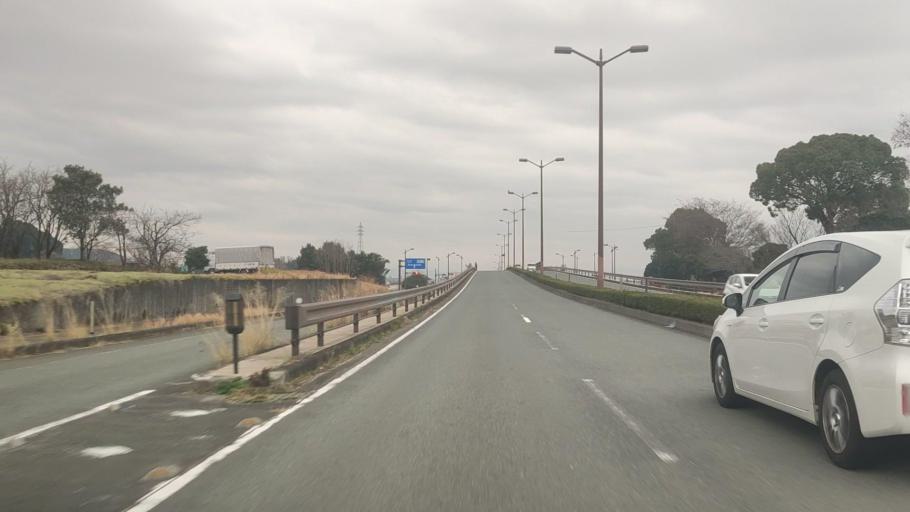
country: JP
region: Kumamoto
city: Ozu
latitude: 32.8376
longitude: 130.8036
